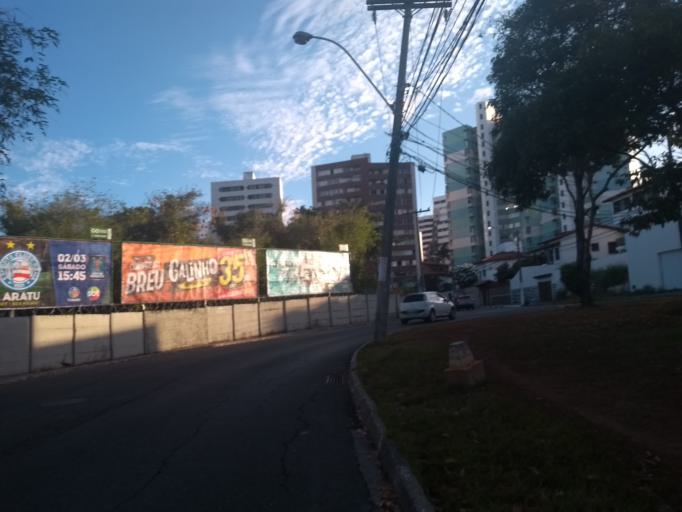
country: BR
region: Bahia
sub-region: Salvador
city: Salvador
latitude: -12.9958
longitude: -38.4597
